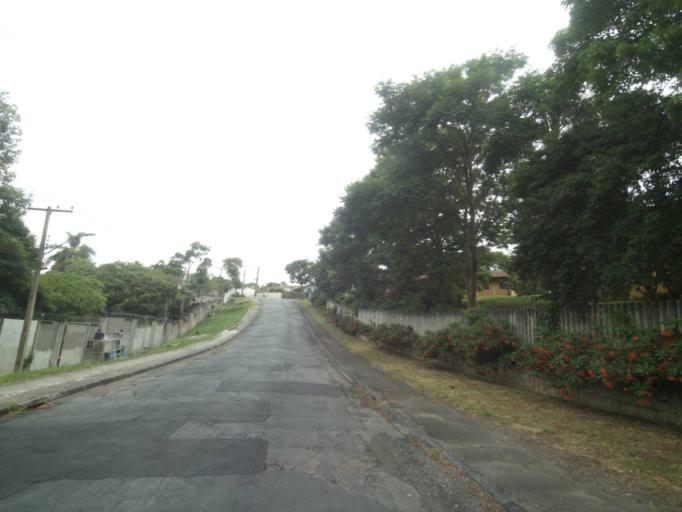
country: BR
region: Parana
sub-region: Curitiba
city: Curitiba
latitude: -25.4116
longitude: -49.3053
